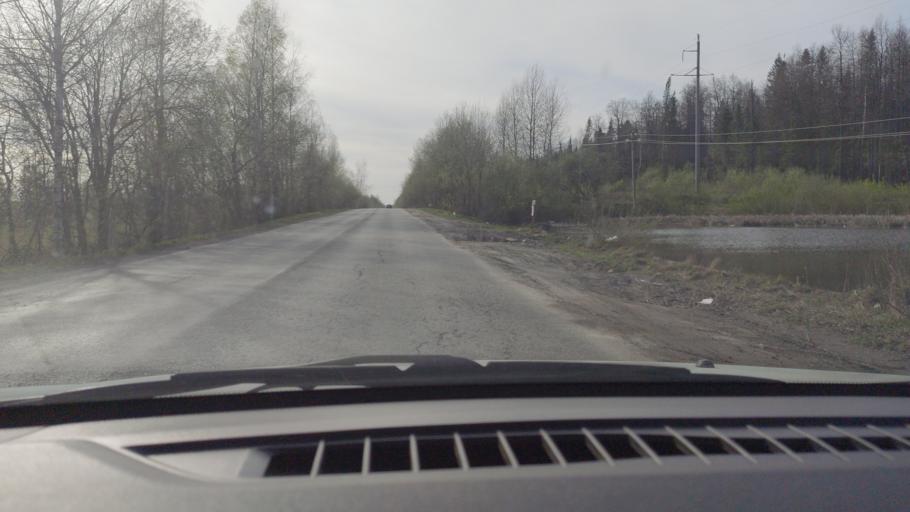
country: RU
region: Perm
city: Ferma
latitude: 57.9420
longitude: 56.4362
